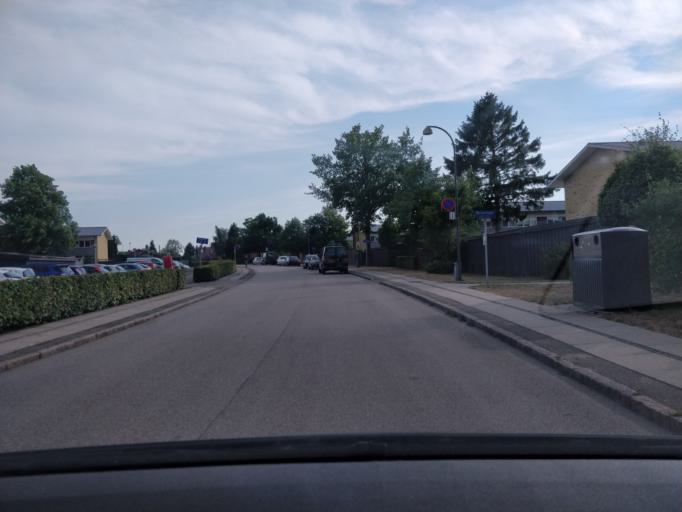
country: DK
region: Capital Region
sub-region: Herlev Kommune
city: Herlev
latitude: 55.7308
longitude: 12.4236
